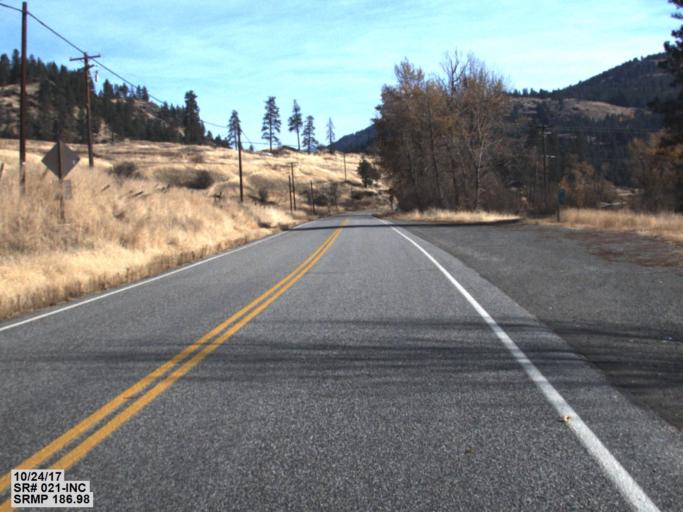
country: CA
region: British Columbia
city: Grand Forks
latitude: 48.9533
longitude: -118.5470
